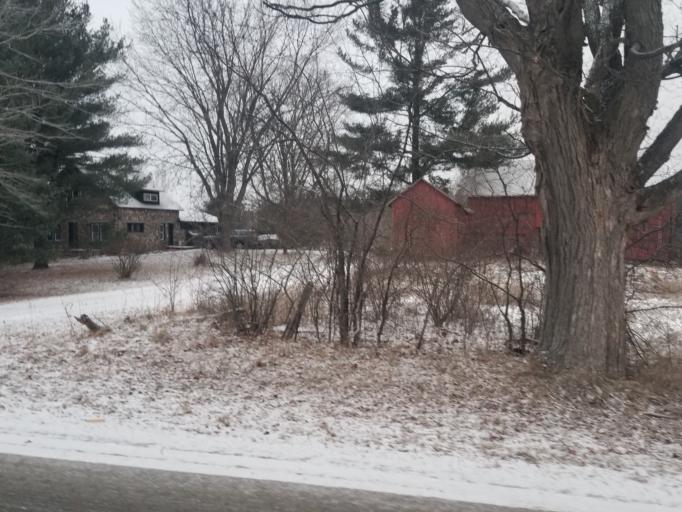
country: US
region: Michigan
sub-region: Osceola County
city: Evart
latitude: 43.8739
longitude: -85.3793
